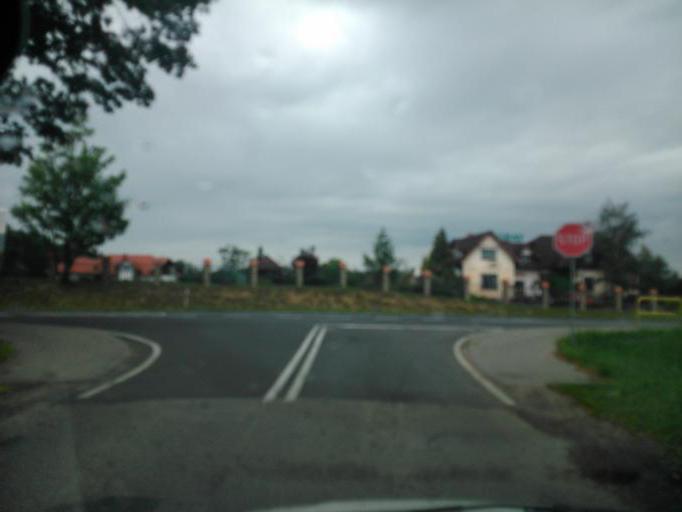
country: PL
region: Kujawsko-Pomorskie
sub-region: Powiat brodnicki
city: Brodnica
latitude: 53.2591
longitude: 19.3580
